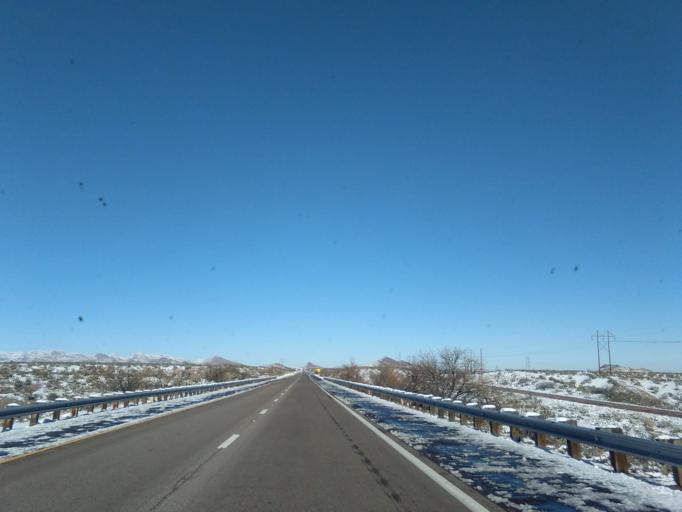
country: US
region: New Mexico
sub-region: Socorro County
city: Socorro
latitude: 33.7090
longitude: -107.0408
